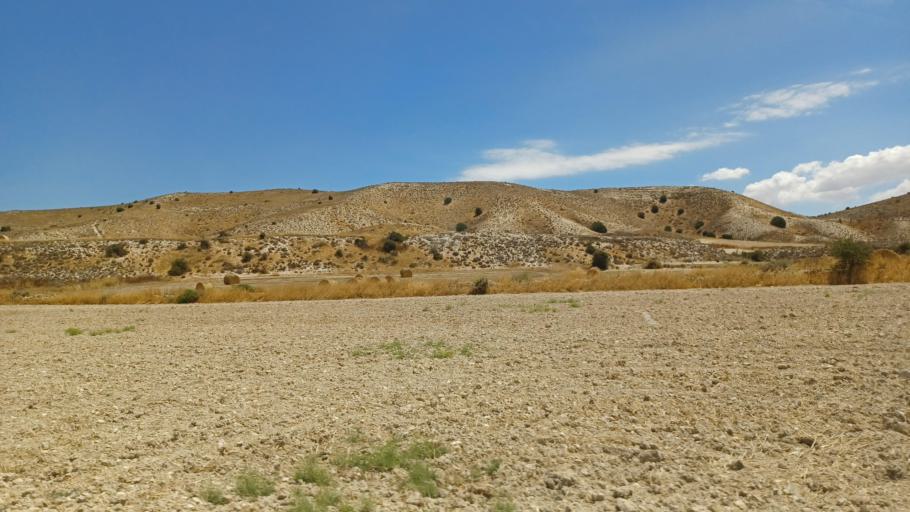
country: CY
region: Larnaka
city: Troulloi
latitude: 35.0426
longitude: 33.6231
